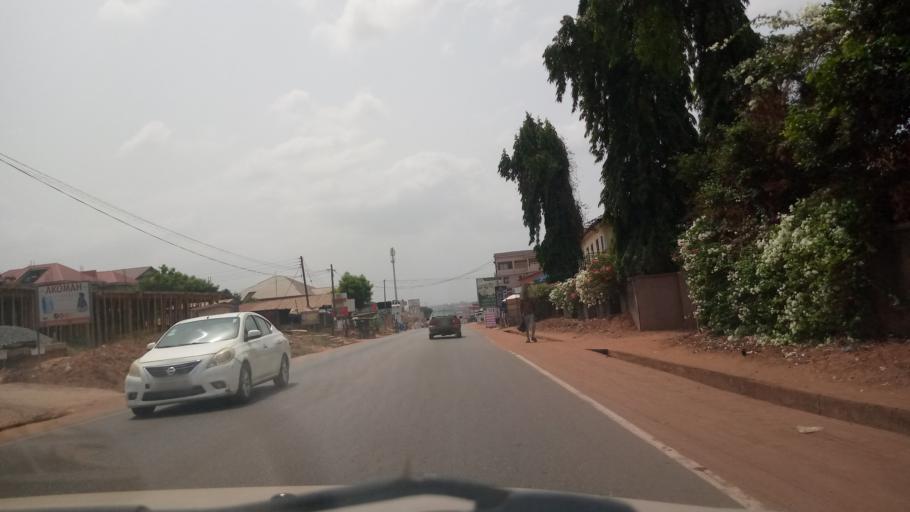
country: GH
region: Greater Accra
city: Medina Estates
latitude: 5.6841
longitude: -0.1936
